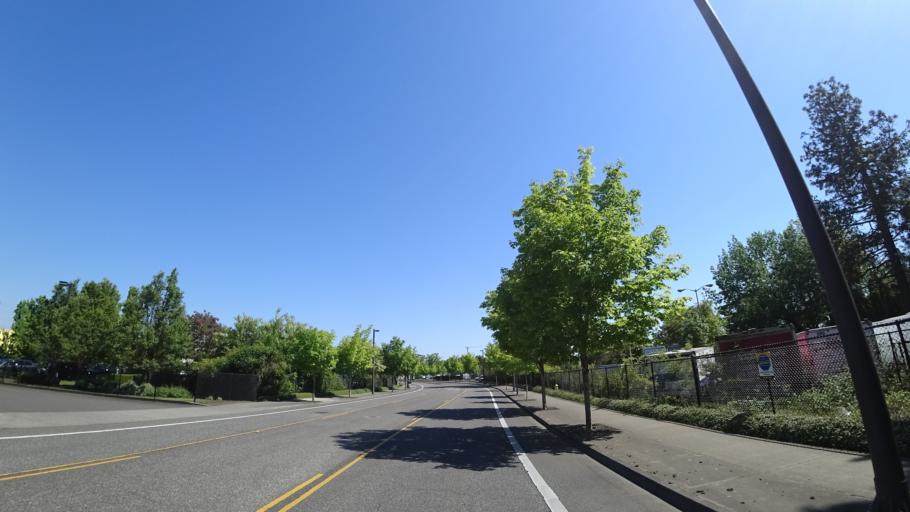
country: US
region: Oregon
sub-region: Washington County
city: Beaverton
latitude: 45.4909
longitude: -122.8137
